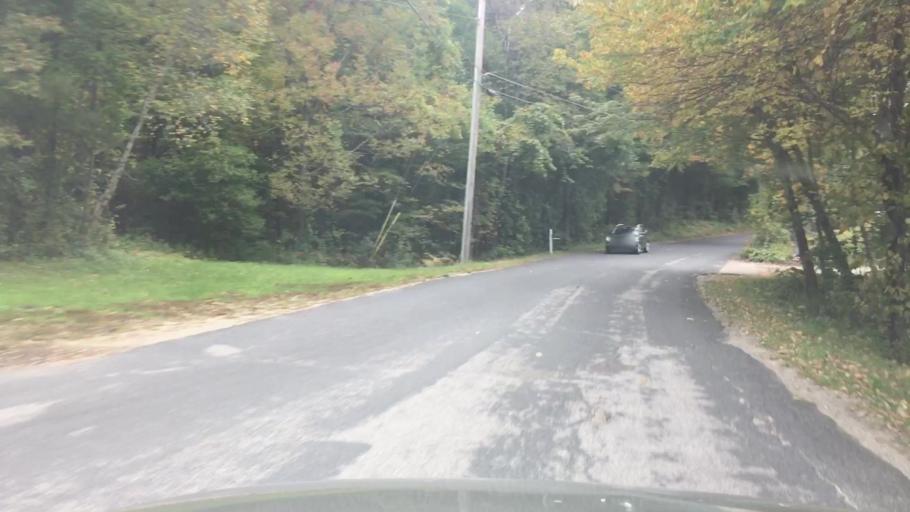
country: US
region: Massachusetts
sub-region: Worcester County
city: Charlton
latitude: 42.1311
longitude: -71.9632
